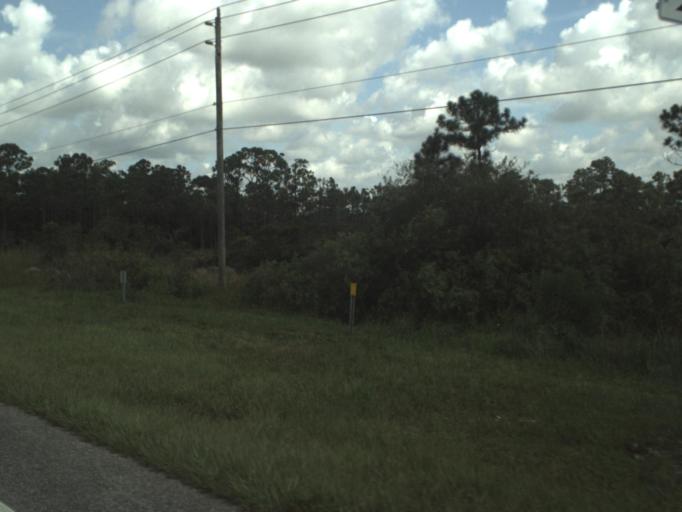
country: US
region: Florida
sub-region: Palm Beach County
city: Palm Beach Gardens
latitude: 26.8049
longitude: -80.1446
